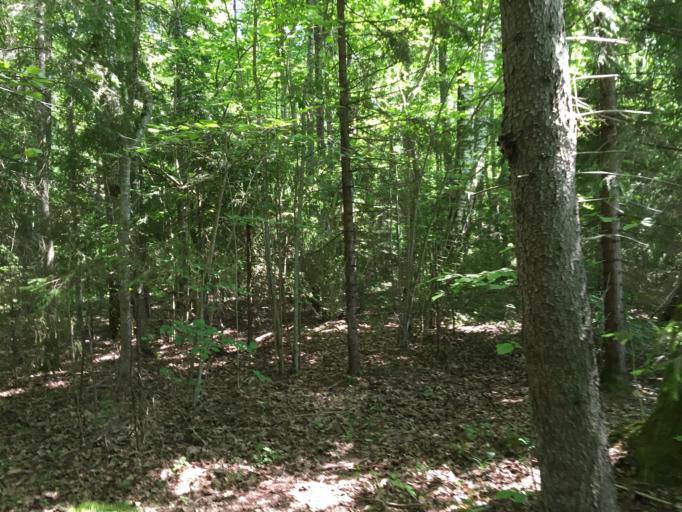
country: LV
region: Sigulda
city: Sigulda
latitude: 57.1896
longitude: 24.9315
